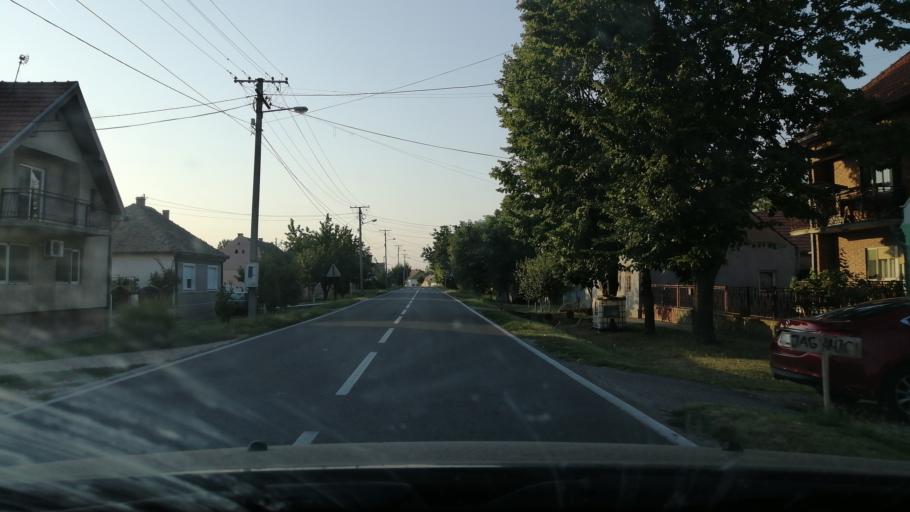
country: RS
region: Central Serbia
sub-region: Belgrade
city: Grocka
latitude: 44.7516
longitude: 20.7488
